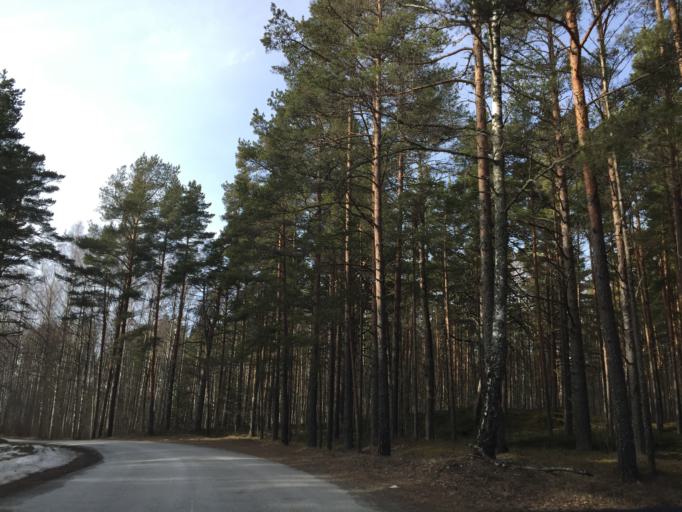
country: EE
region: Paernumaa
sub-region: Paernu linn
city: Parnu
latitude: 58.2410
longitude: 24.5220
